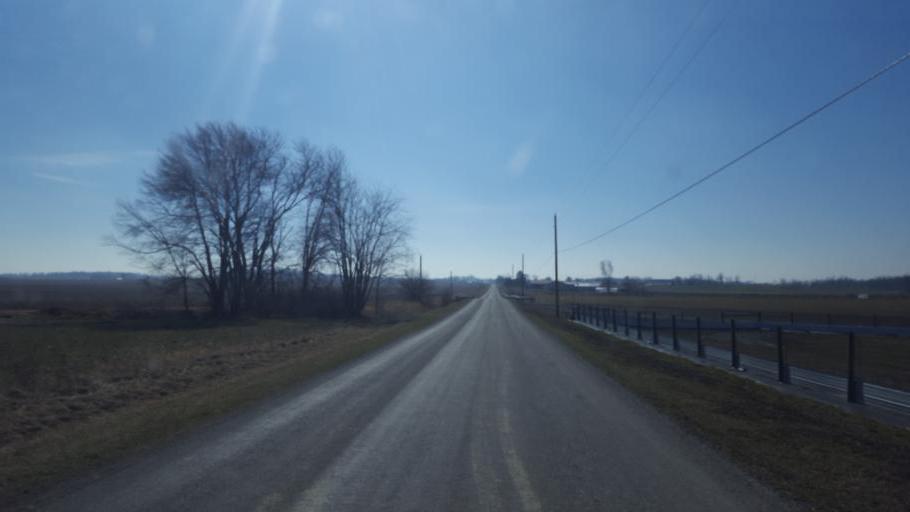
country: US
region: Ohio
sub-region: Huron County
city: Greenwich
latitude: 41.0027
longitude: -82.5830
